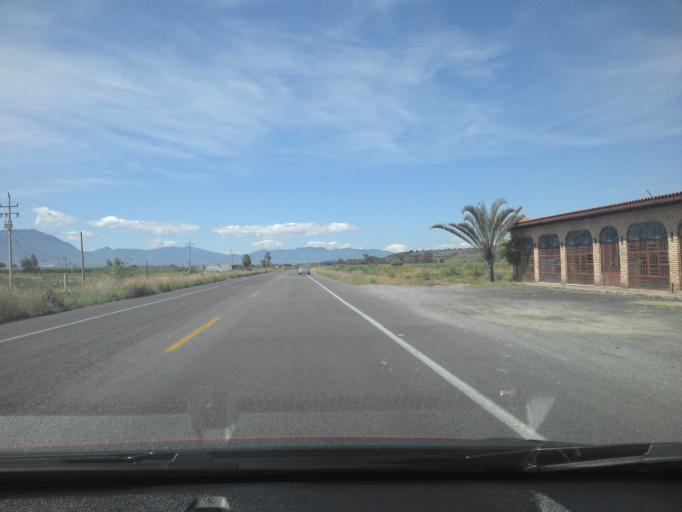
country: MX
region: Jalisco
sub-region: Teuchitlan
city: La Estanzuela
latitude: 20.6695
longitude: -103.7987
